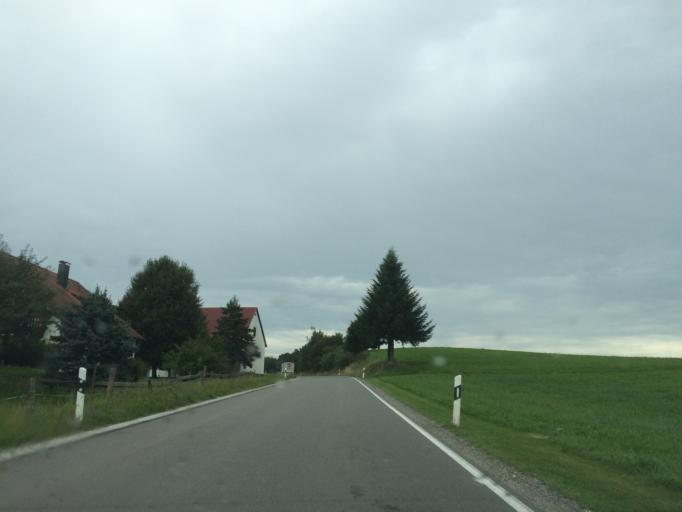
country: DE
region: Baden-Wuerttemberg
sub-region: Tuebingen Region
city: Bad Waldsee
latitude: 47.9516
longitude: 9.7823
